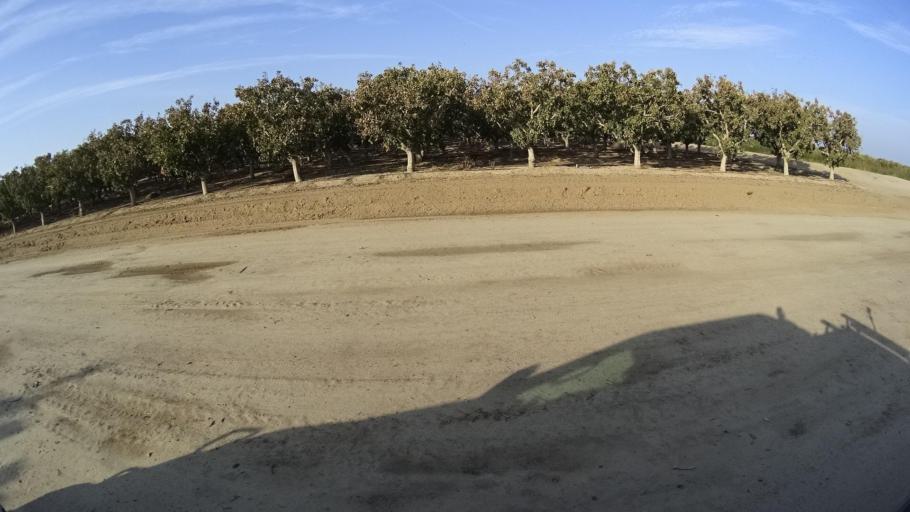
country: US
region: California
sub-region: Kern County
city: McFarland
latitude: 35.7260
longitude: -119.1873
